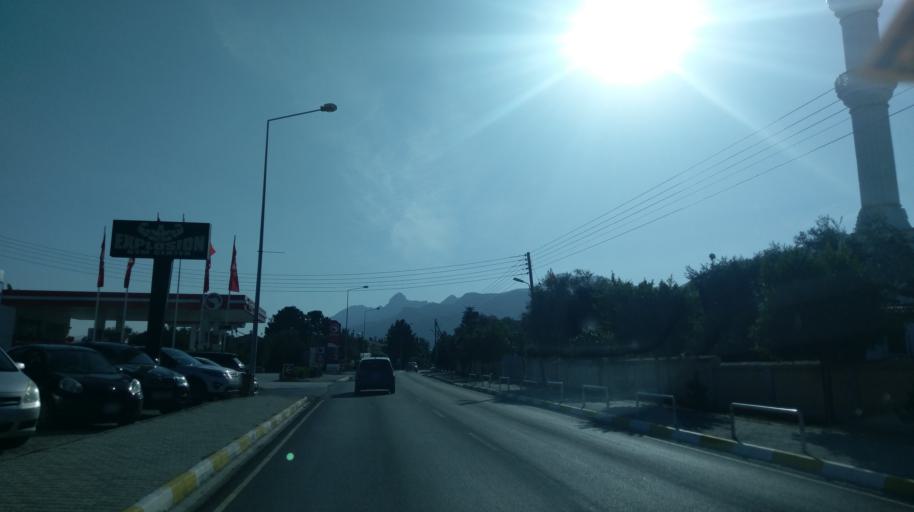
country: CY
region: Keryneia
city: Kyrenia
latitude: 35.3303
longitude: 33.3348
